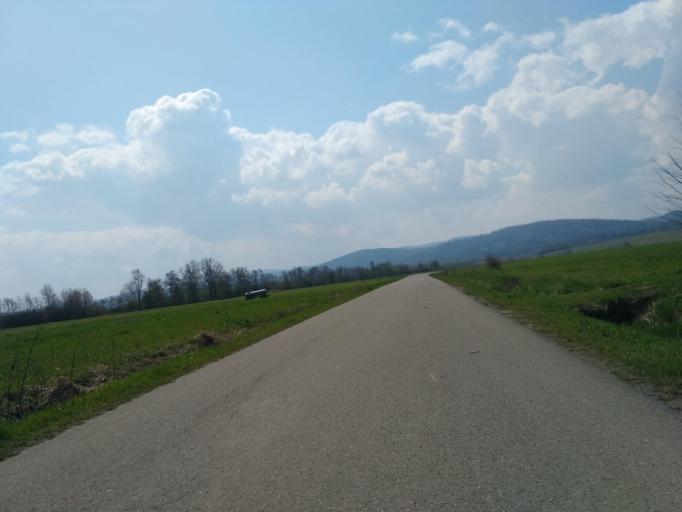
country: PL
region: Subcarpathian Voivodeship
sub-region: Powiat sanocki
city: Besko
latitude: 49.5391
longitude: 21.9766
